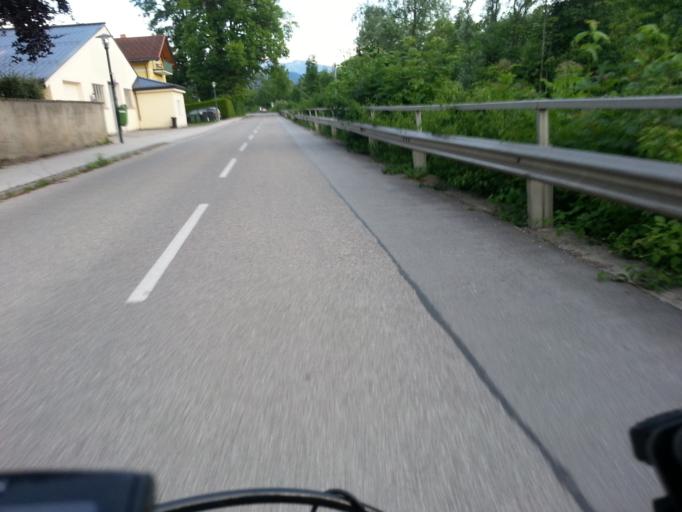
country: AT
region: Salzburg
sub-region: Politischer Bezirk Salzburg-Umgebung
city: Elsbethen
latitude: 47.7695
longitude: 13.0754
